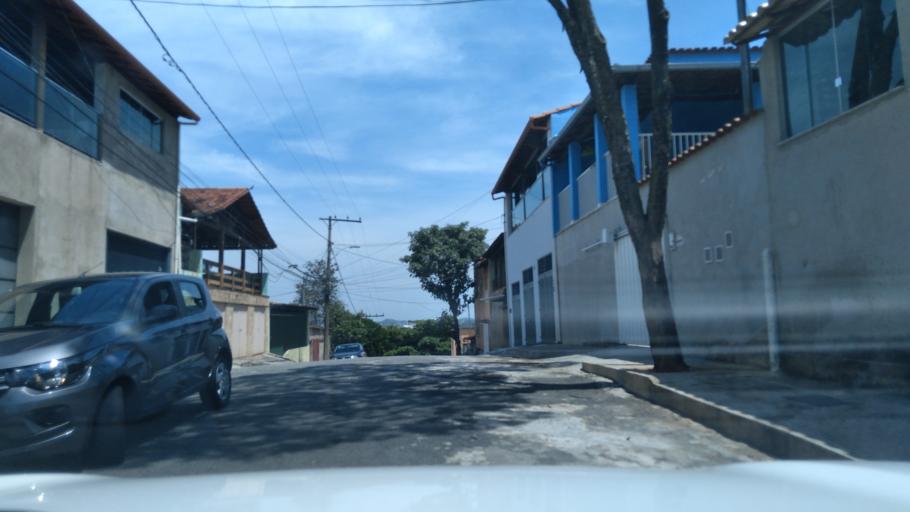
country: BR
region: Minas Gerais
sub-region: Contagem
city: Contagem
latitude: -19.9068
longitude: -44.0148
